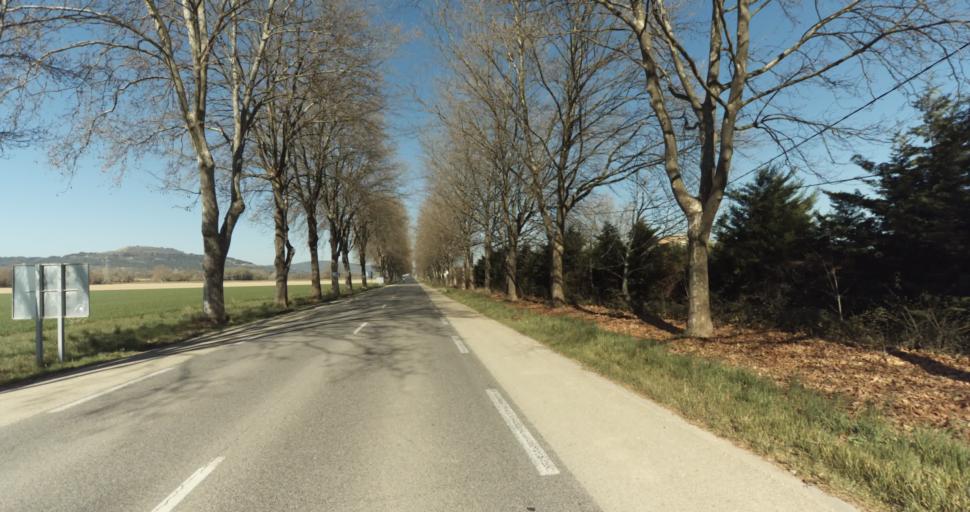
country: FR
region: Provence-Alpes-Cote d'Azur
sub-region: Departement des Bouches-du-Rhone
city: Meyrargues
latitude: 43.6491
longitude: 5.4877
